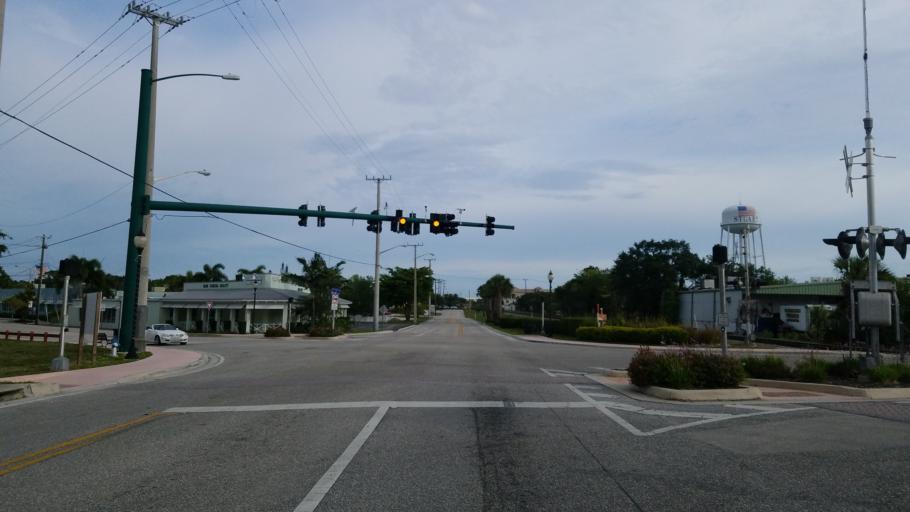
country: US
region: Florida
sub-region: Martin County
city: Stuart
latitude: 27.1936
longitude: -80.2491
